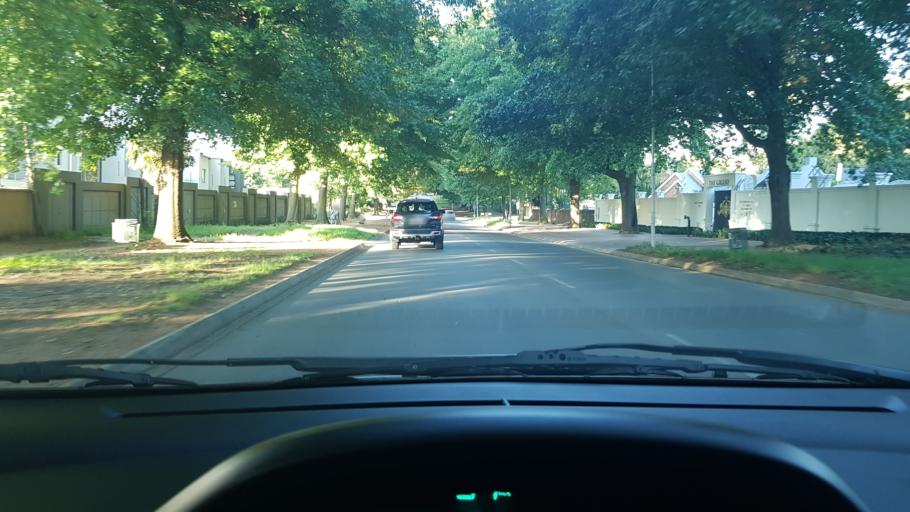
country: ZA
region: Gauteng
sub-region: Ekurhuleni Metropolitan Municipality
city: Germiston
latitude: -26.1748
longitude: 28.1405
